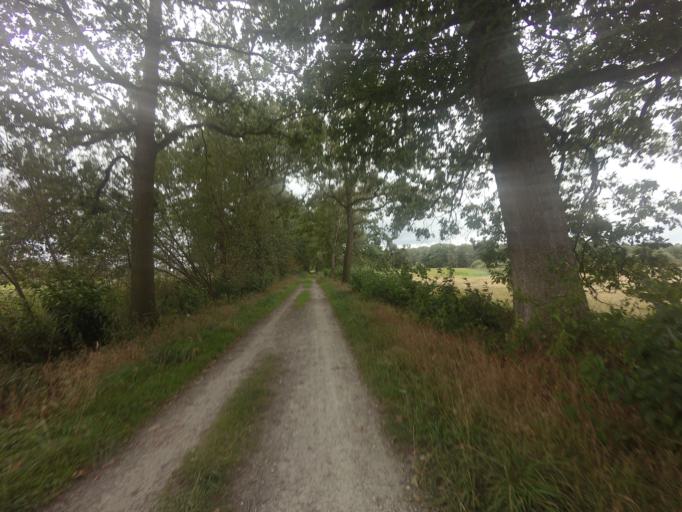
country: NL
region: Drenthe
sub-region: Gemeente Westerveld
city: Dwingeloo
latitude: 52.8928
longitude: 6.2643
